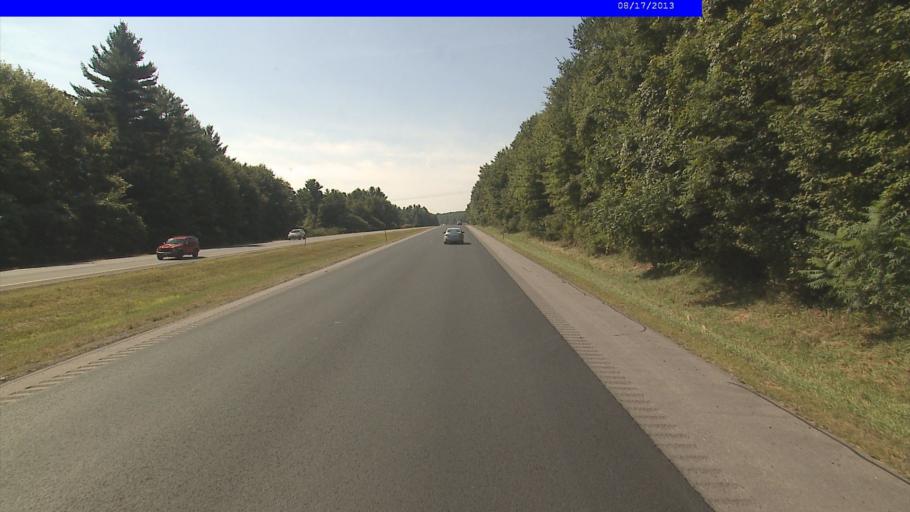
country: US
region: New Hampshire
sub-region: Cheshire County
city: Westmoreland
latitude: 43.0309
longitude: -72.4702
